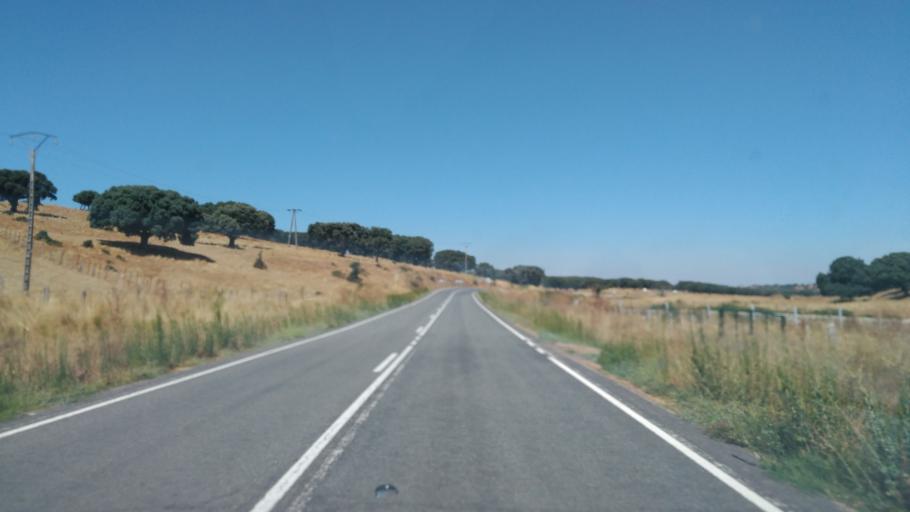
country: ES
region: Castille and Leon
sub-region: Provincia de Salamanca
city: Matilla de los Canos del Rio
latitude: 40.7991
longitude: -5.9214
